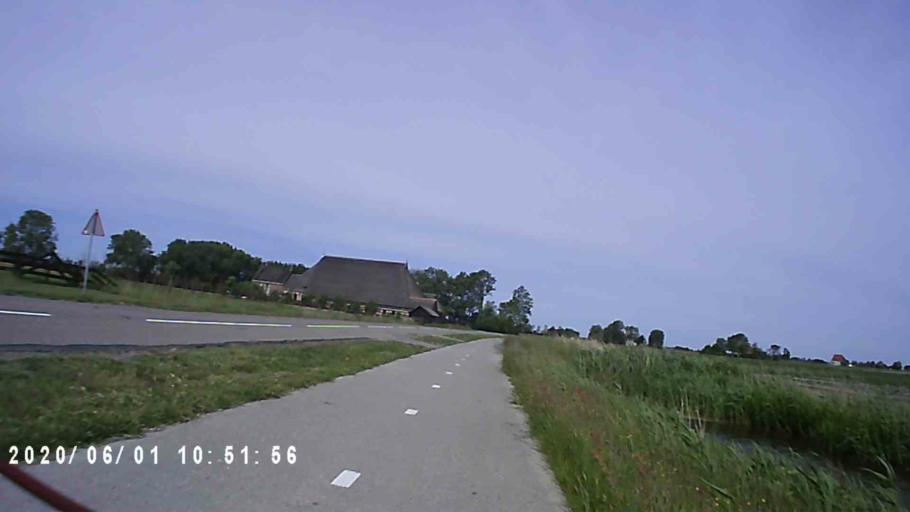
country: NL
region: Friesland
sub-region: Gemeente Franekeradeel
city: Franeker
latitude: 53.1988
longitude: 5.5204
